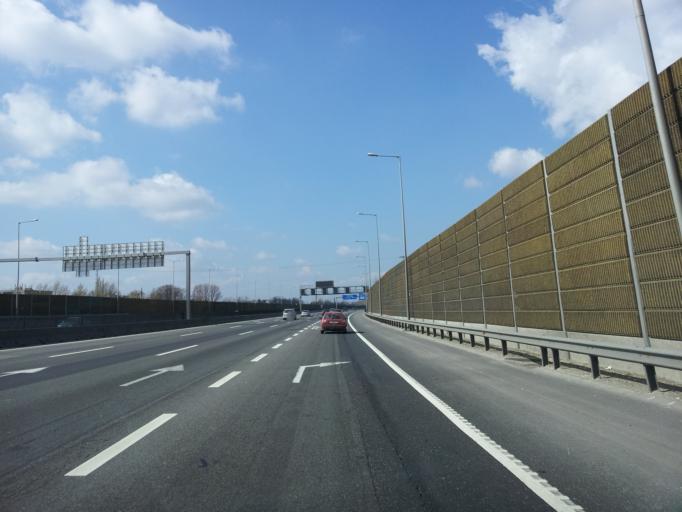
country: HU
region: Pest
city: Halasztelek
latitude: 47.3994
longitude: 18.9966
